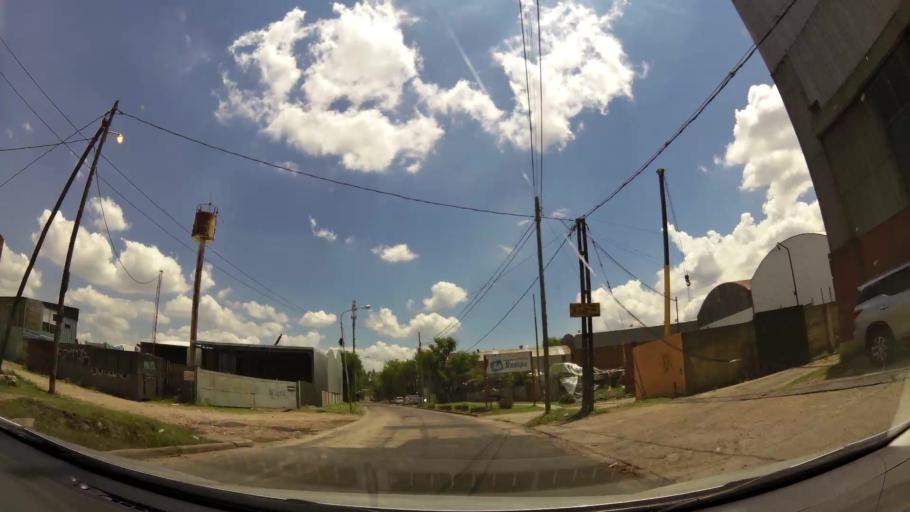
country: AR
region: Buenos Aires
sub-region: Partido de Tigre
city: Tigre
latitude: -34.4042
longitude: -58.5999
